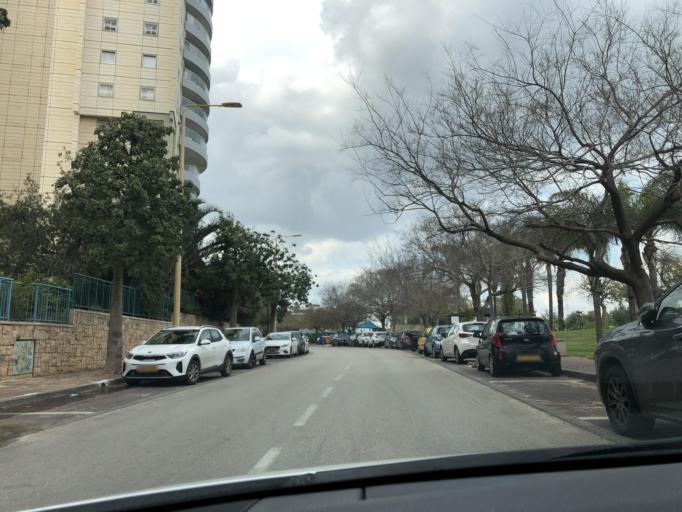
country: IL
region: Central District
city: Ganne Tiqwa
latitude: 32.0607
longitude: 34.8822
